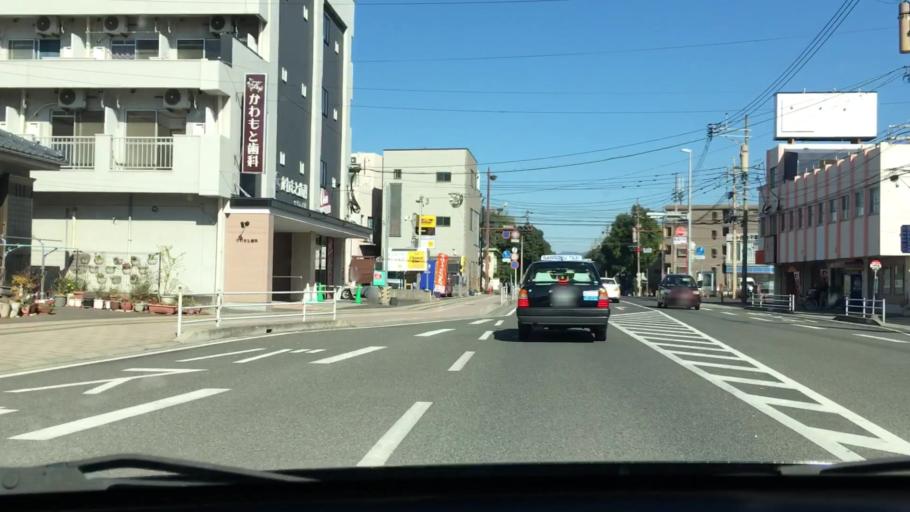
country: JP
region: Kagoshima
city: Kagoshima-shi
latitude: 31.5642
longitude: 130.5451
